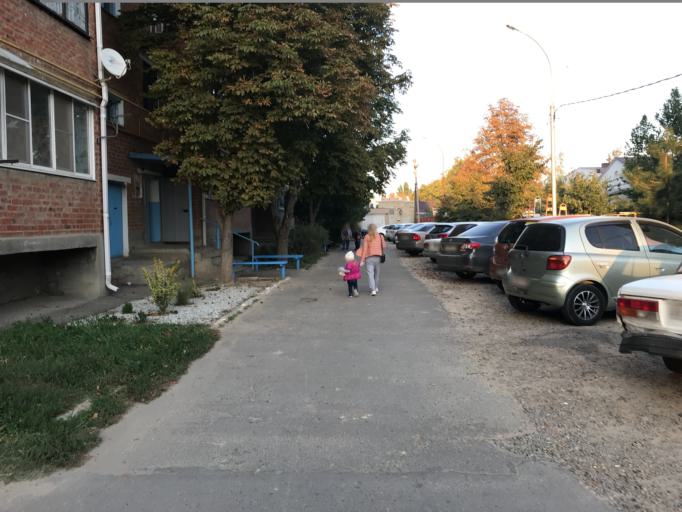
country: RU
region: Krasnodarskiy
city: Slavyansk-na-Kubani
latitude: 45.2586
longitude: 38.1220
